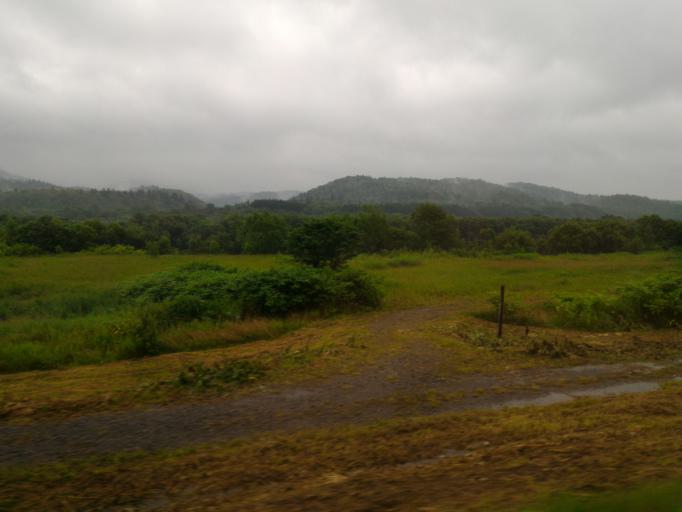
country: JP
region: Hokkaido
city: Nayoro
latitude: 44.7610
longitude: 142.0518
